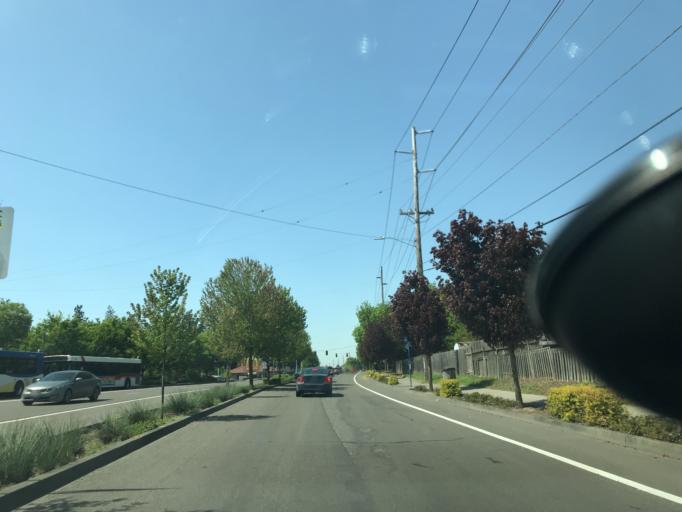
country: US
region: Oregon
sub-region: Multnomah County
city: Gresham
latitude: 45.4897
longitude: -122.4729
